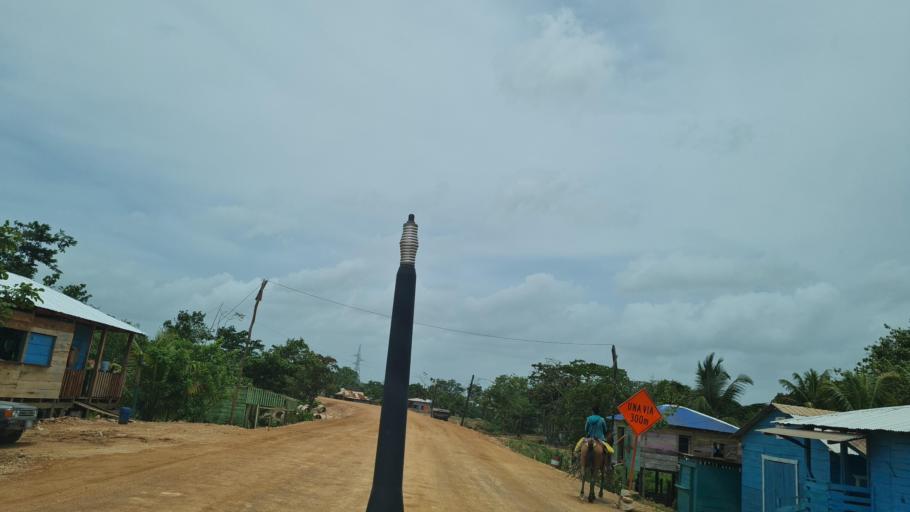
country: NI
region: Atlantico Norte (RAAN)
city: Bonanza
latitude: 14.0391
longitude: -84.0761
